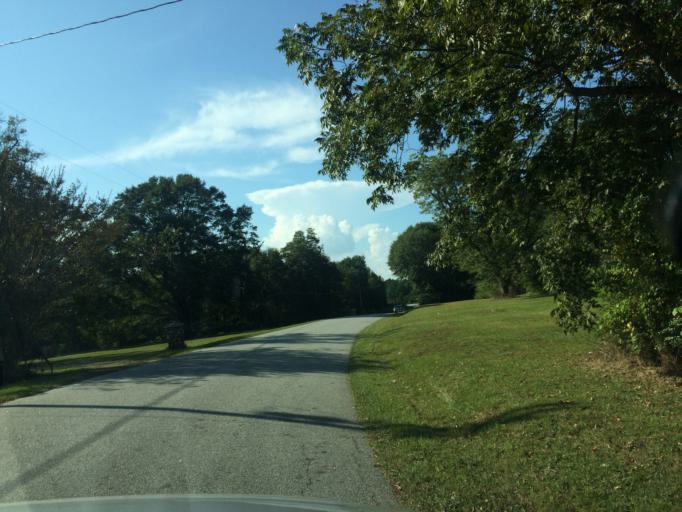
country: US
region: South Carolina
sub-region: Laurens County
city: Laurens
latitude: 34.5753
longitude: -82.0923
